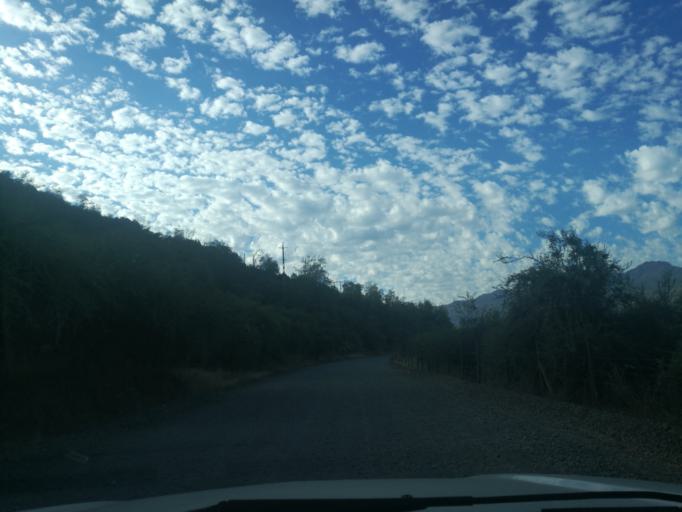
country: CL
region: O'Higgins
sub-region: Provincia de Cachapoal
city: Machali
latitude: -34.2442
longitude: -70.4698
